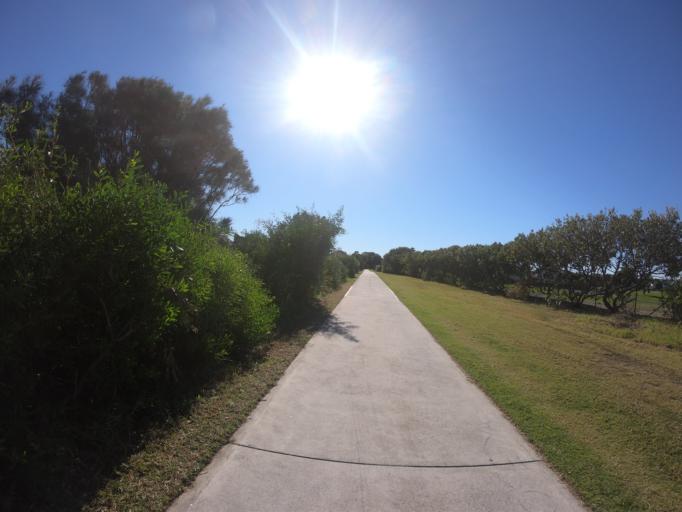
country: AU
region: New South Wales
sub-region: Wollongong
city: Fairy Meadow
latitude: -34.3930
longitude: 150.9056
